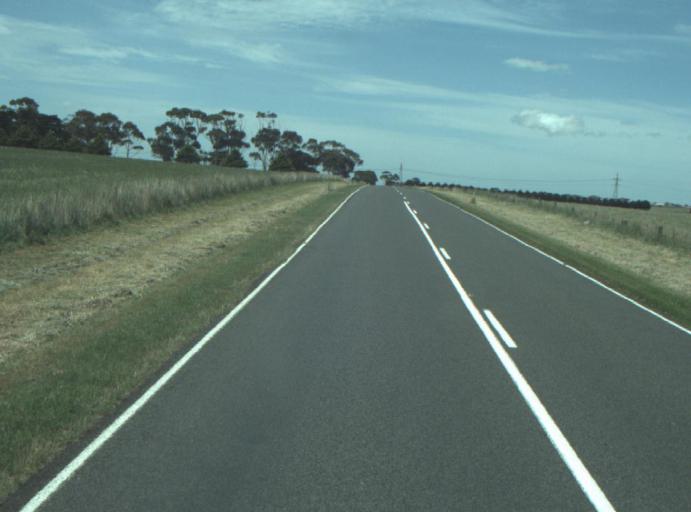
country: AU
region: Victoria
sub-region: Greater Geelong
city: Bell Post Hill
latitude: -38.0084
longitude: 144.2987
